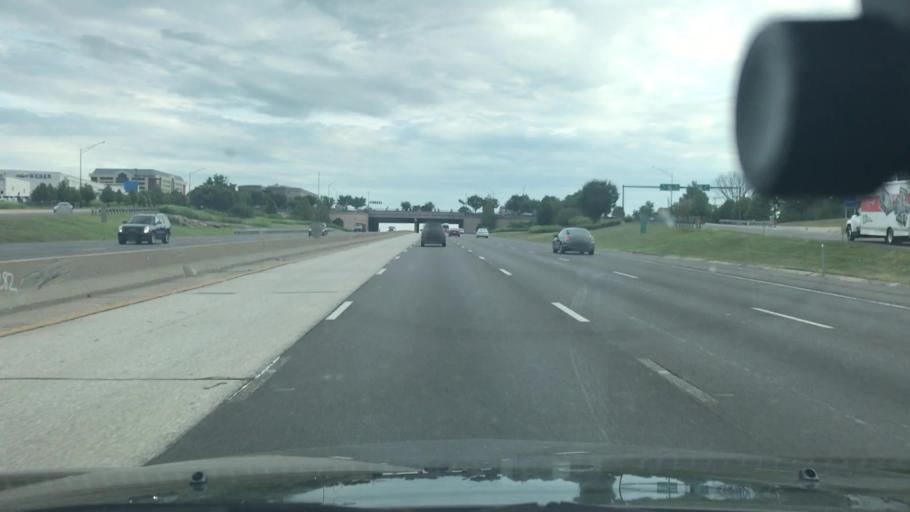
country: US
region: Missouri
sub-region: Saint Louis County
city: Creve Coeur
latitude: 38.6756
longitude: -90.4495
